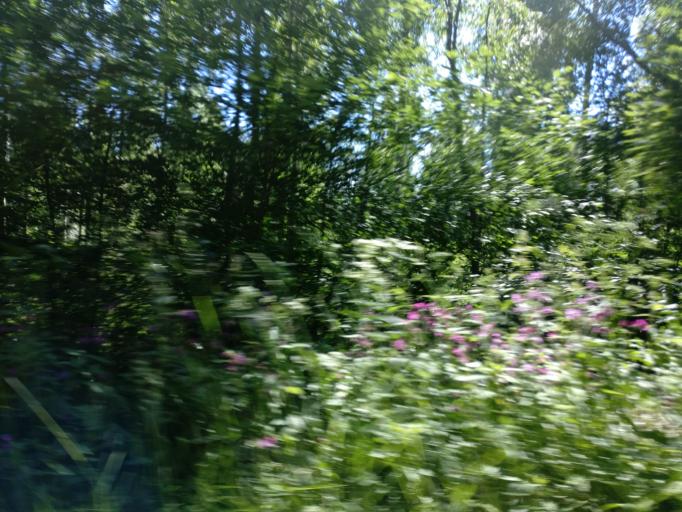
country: FI
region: Southern Savonia
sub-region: Savonlinna
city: Rantasalmi
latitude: 62.1654
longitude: 28.2488
